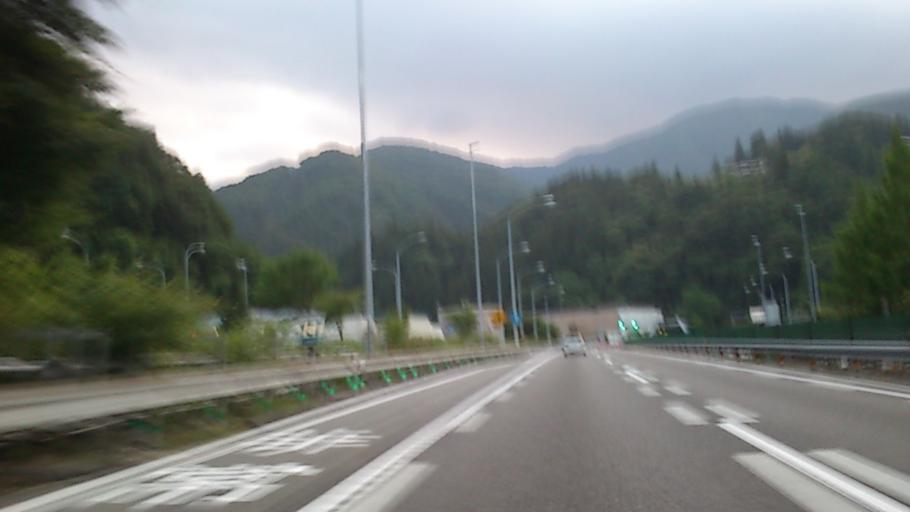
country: JP
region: Nagano
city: Iida
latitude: 35.4575
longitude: 137.6763
